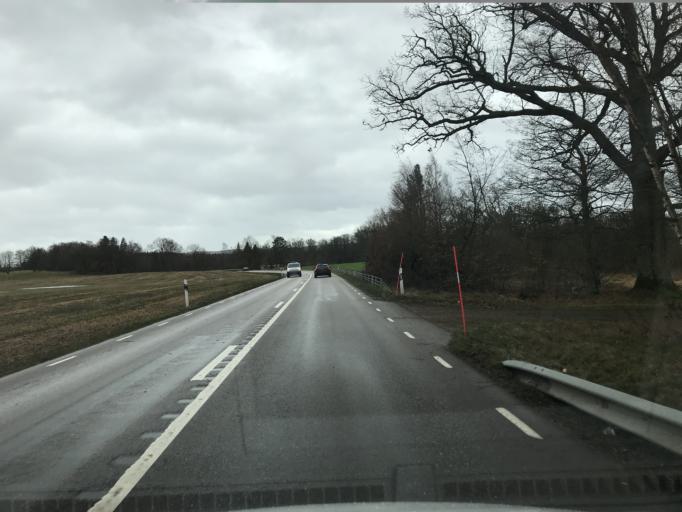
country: SE
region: Skane
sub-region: Klippans Kommun
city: Klippan
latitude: 56.1058
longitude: 13.1770
